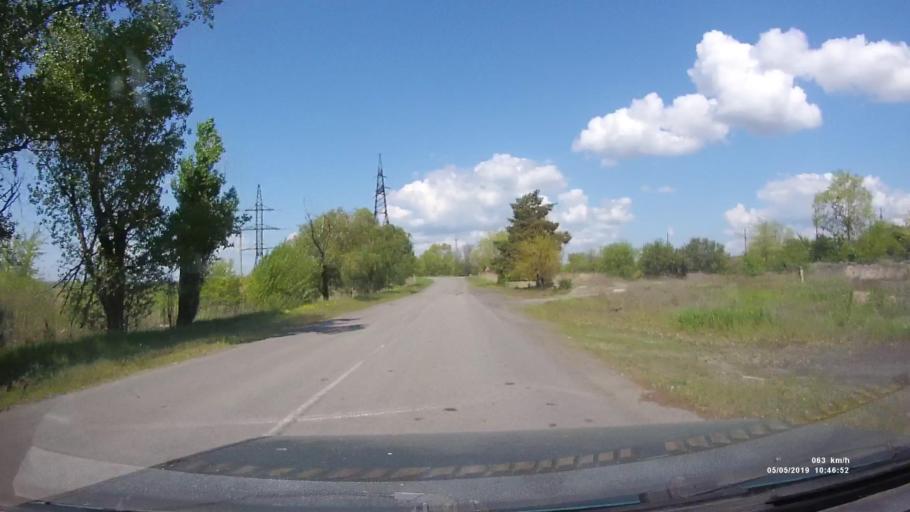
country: RU
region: Rostov
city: Ust'-Donetskiy
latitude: 47.6366
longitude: 40.8397
